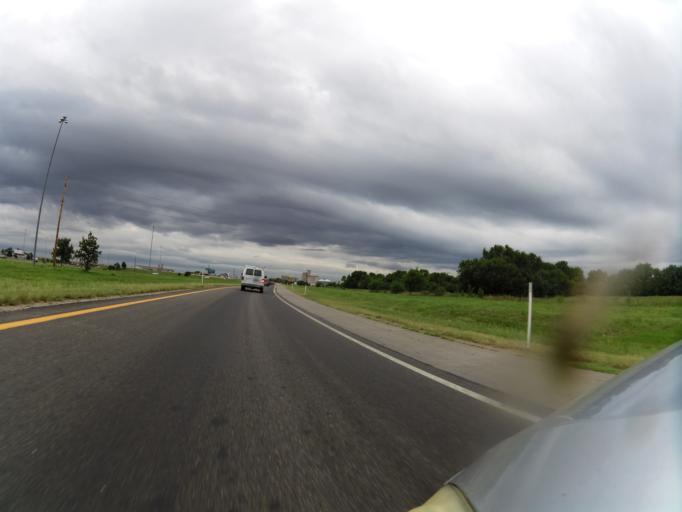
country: US
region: Kansas
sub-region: Sedgwick County
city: Park City
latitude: 37.7489
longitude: -97.3200
